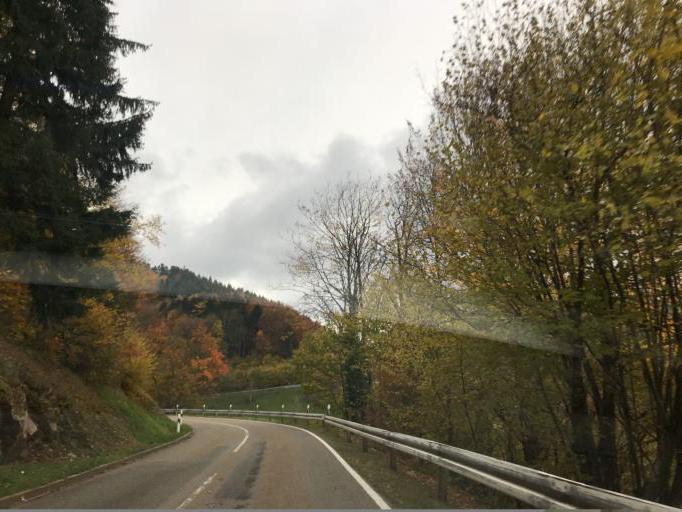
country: DE
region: Baden-Wuerttemberg
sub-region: Freiburg Region
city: Wieden
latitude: 47.8800
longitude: 7.8449
